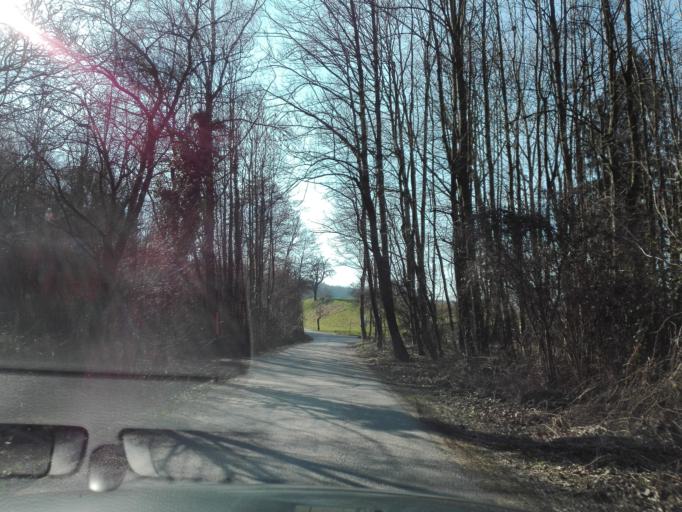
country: AT
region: Upper Austria
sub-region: Wels-Land
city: Holzhausen
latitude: 48.2533
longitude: 14.0819
